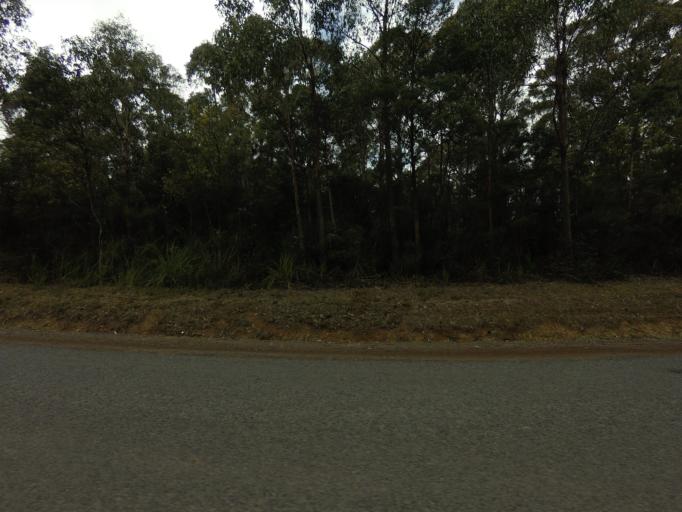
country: AU
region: Tasmania
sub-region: Huon Valley
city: Geeveston
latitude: -43.4191
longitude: 146.9076
